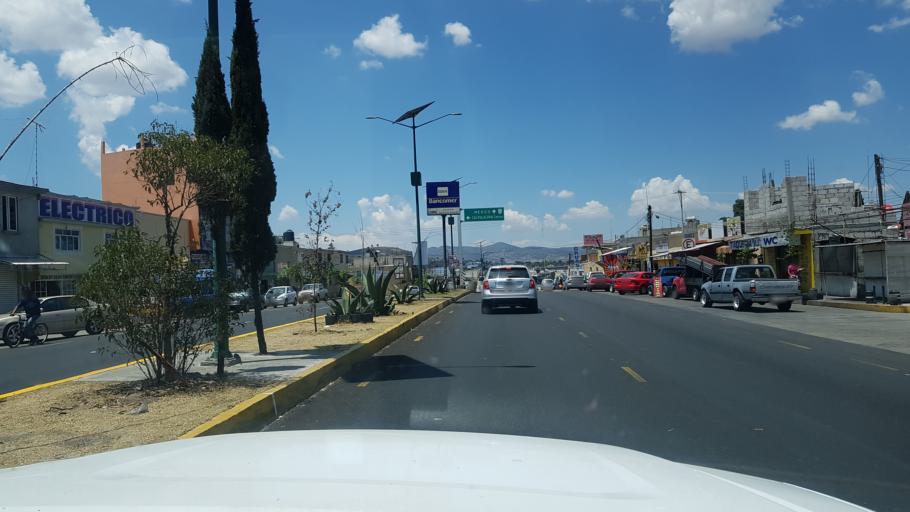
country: MX
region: Hidalgo
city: Calpulalpan
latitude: 19.5921
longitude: -98.5661
